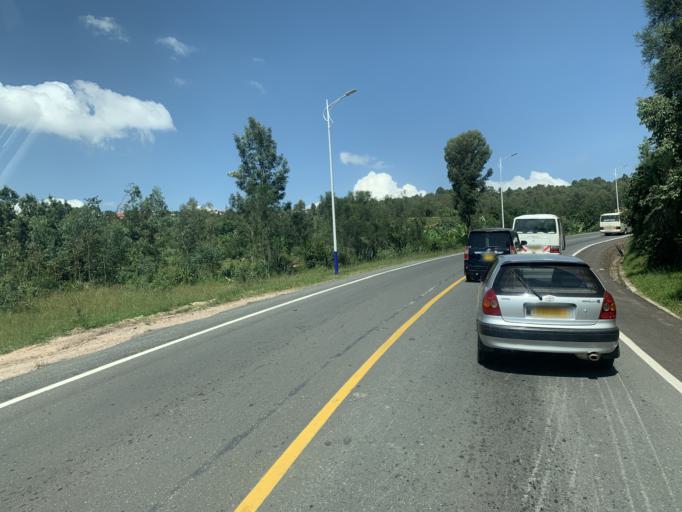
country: RW
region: Southern Province
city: Gitarama
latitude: -2.0570
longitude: 29.8034
